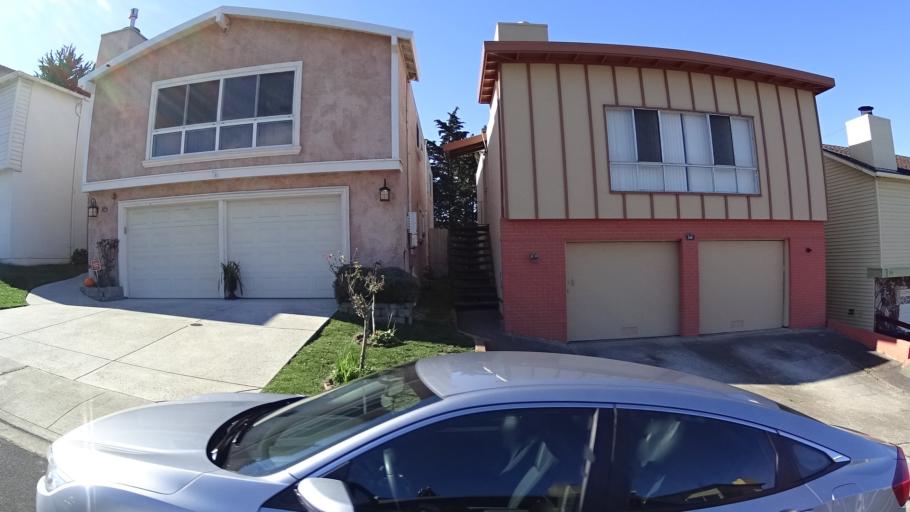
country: US
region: California
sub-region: San Mateo County
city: Colma
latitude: 37.6561
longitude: -122.4686
